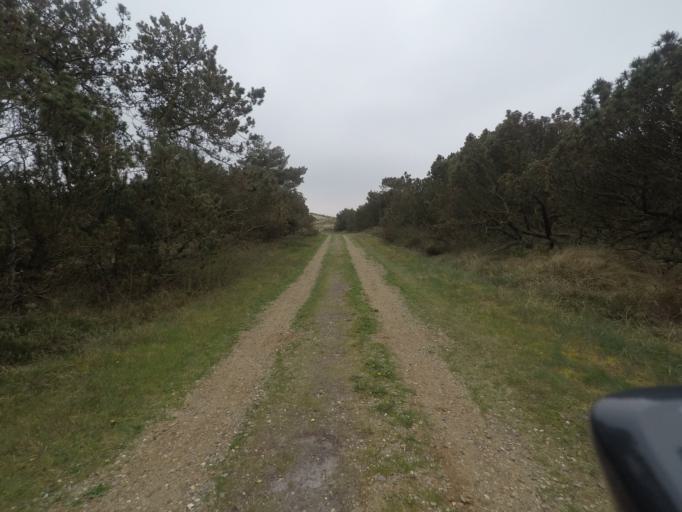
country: DE
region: Schleswig-Holstein
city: List
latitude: 55.1187
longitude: 8.5201
